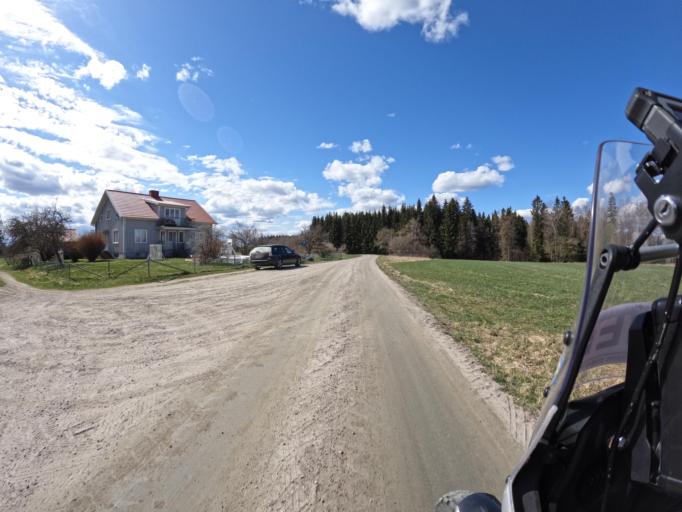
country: SE
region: Vaestra Goetaland
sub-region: Ulricehamns Kommun
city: Ulricehamn
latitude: 57.9041
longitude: 13.3997
